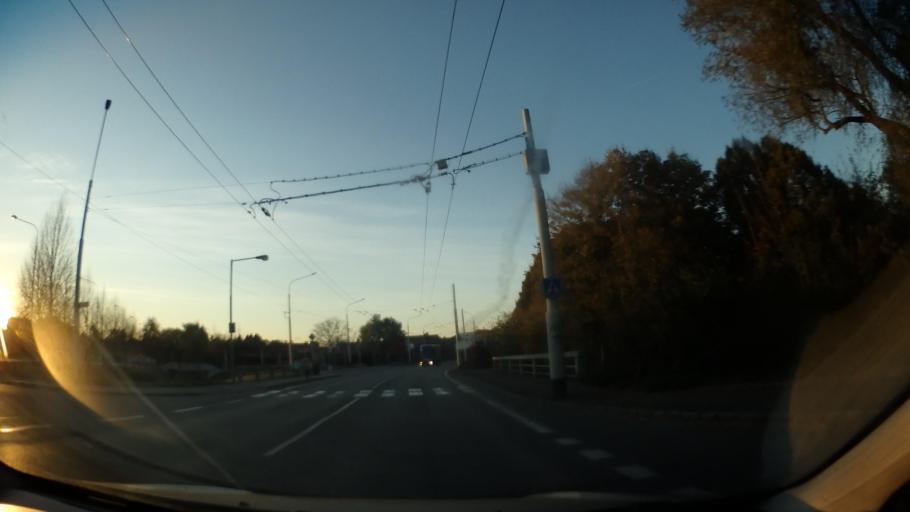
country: CZ
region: Pardubicky
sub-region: Okres Pardubice
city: Lazne Bohdanec
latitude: 50.0729
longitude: 15.6828
